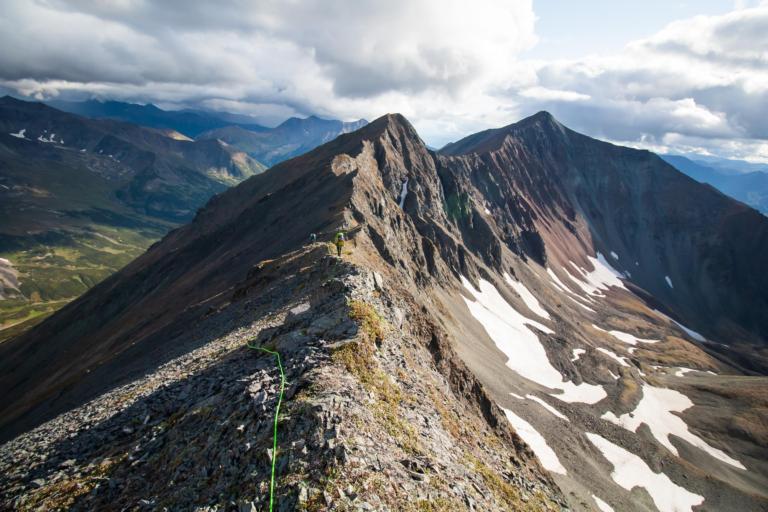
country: RU
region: Kamtsjatka
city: Yelizovo
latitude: 53.8500
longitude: 158.1897
